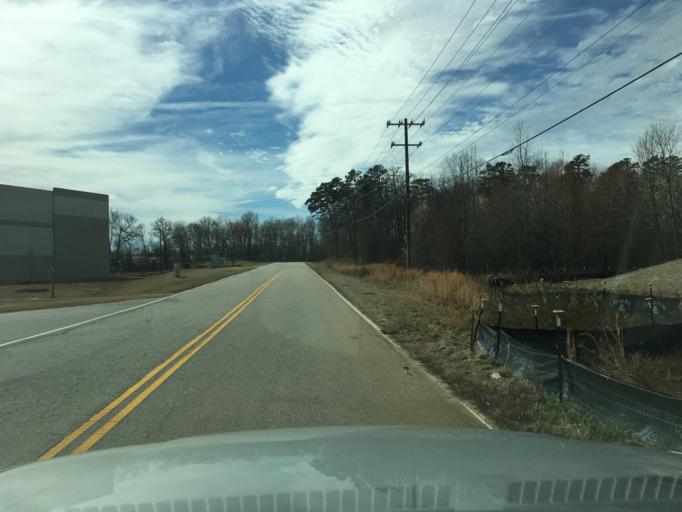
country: US
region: South Carolina
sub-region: Spartanburg County
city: Duncan
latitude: 34.9045
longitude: -82.1622
